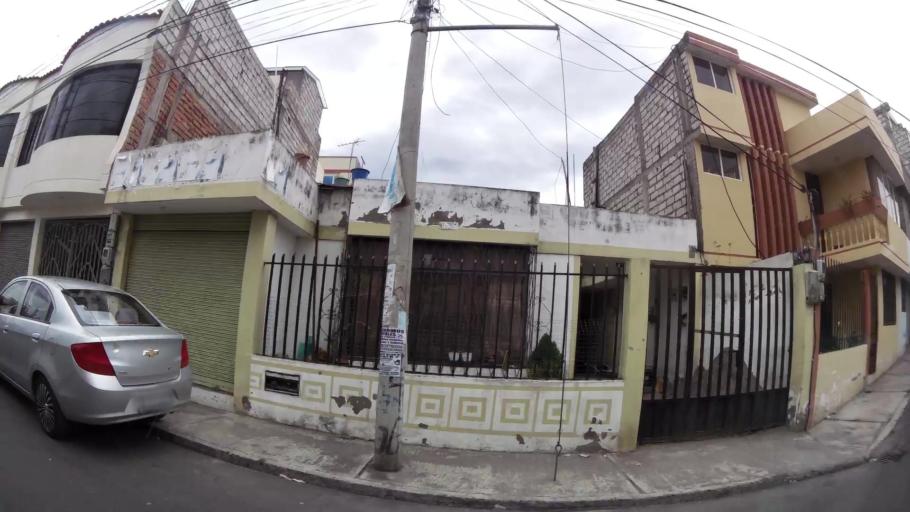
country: EC
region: Cotopaxi
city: Latacunga
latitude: -0.9368
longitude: -78.6215
